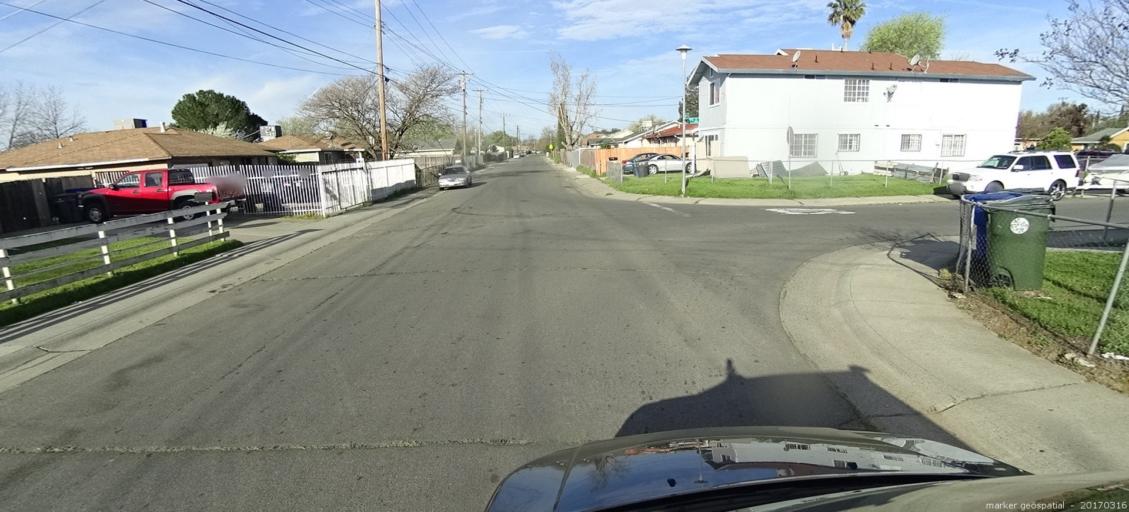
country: US
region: California
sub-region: Sacramento County
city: Parkway
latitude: 38.5031
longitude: -121.4762
